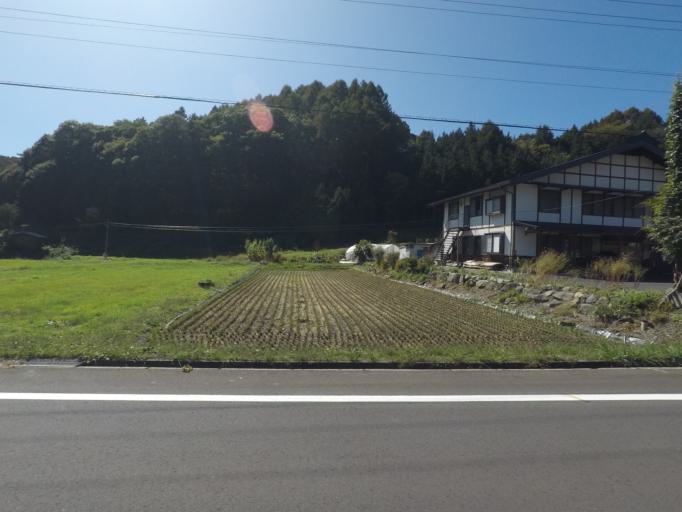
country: JP
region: Nagano
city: Tatsuno
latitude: 35.9720
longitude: 137.7550
